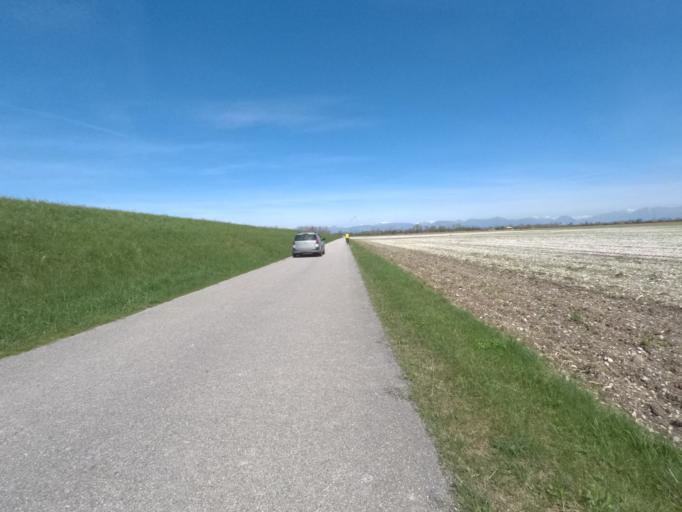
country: IT
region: Friuli Venezia Giulia
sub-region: Provincia di Udine
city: Camino al Tagliamento
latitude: 45.9516
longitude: 12.9150
